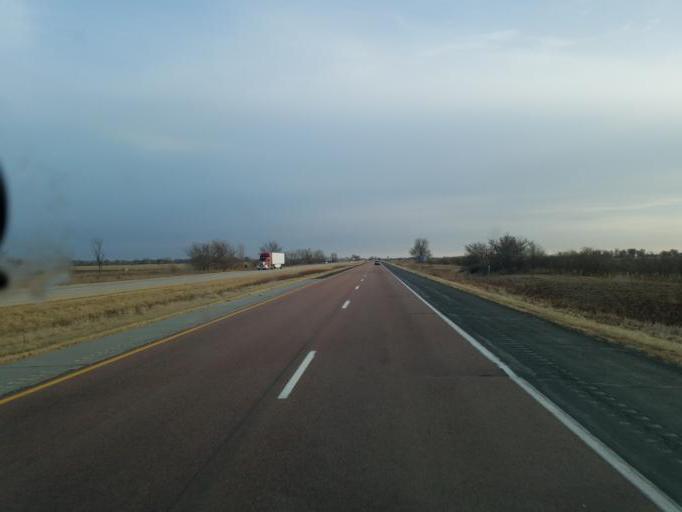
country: US
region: Iowa
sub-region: Monona County
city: Onawa
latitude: 42.0211
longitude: -96.1279
